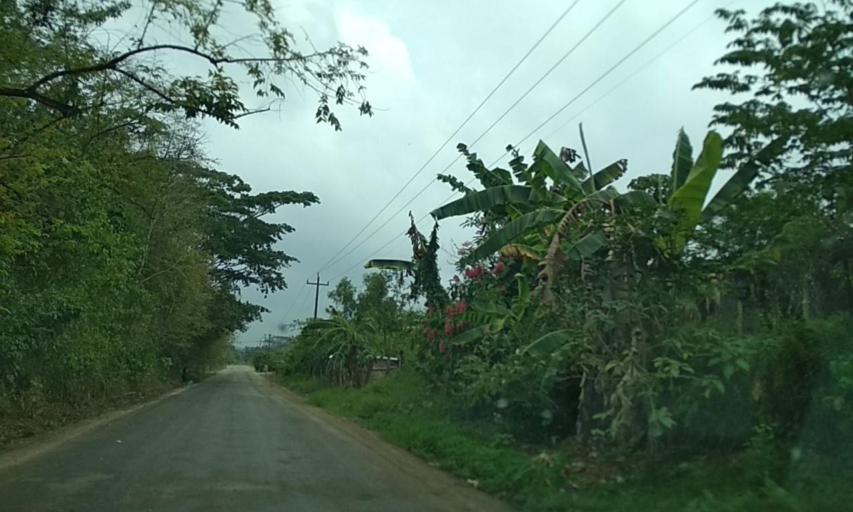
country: MX
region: Tabasco
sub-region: Huimanguillo
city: Francisco Rueda
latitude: 17.5884
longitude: -94.0922
